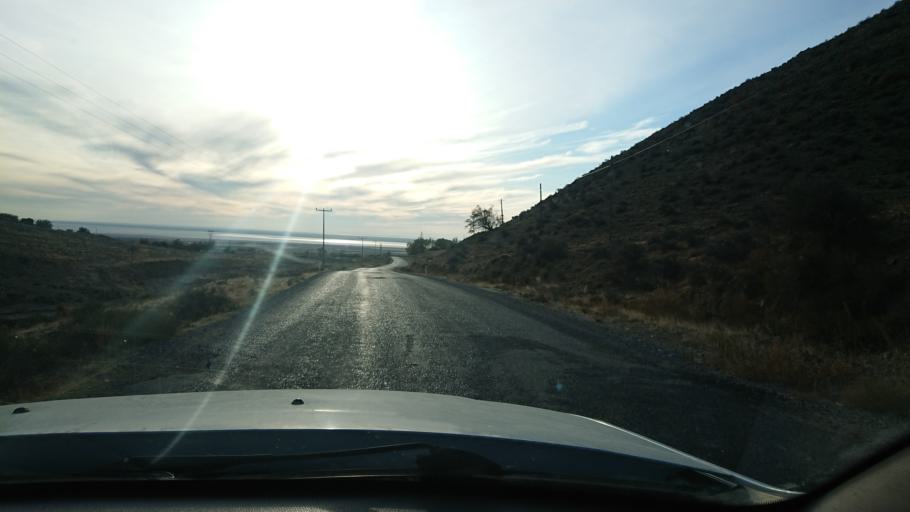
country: TR
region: Ankara
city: Sereflikochisar
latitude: 38.7472
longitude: 33.6844
